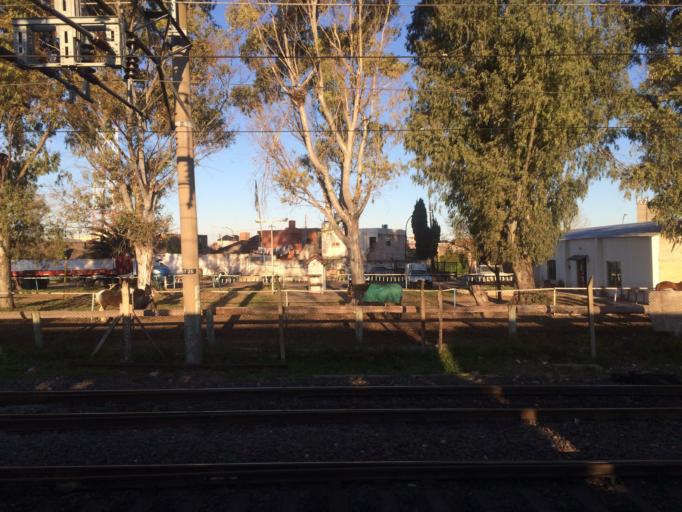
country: AR
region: Buenos Aires
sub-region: Partido de Lanus
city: Lanus
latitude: -34.6958
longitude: -58.3863
